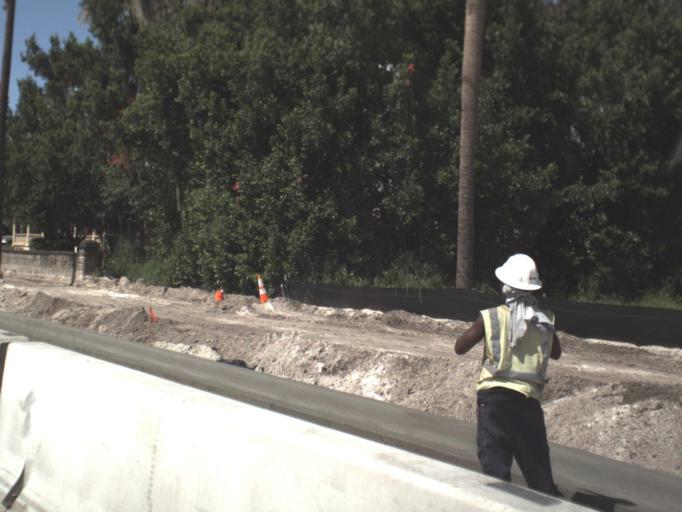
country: US
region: Florida
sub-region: DeSoto County
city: Arcadia
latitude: 27.2181
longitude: -81.8645
